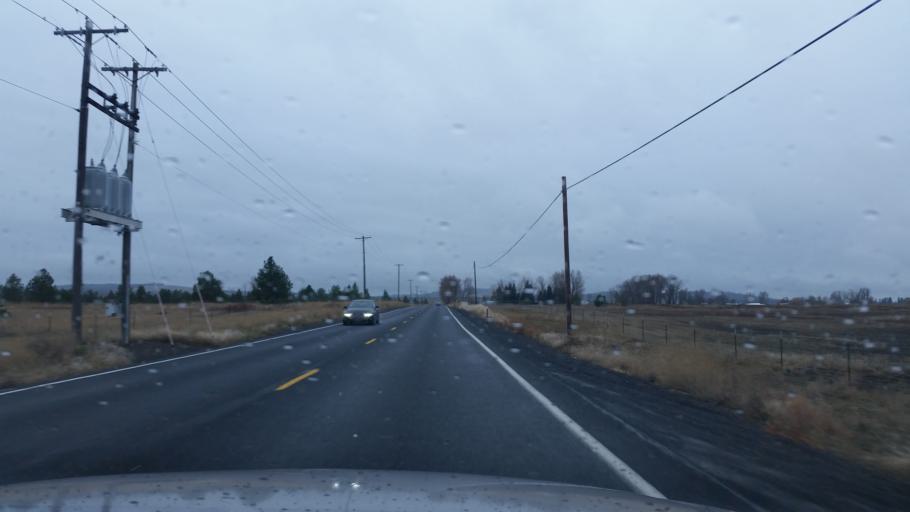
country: US
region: Washington
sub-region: Spokane County
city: Airway Heights
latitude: 47.6267
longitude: -117.6041
